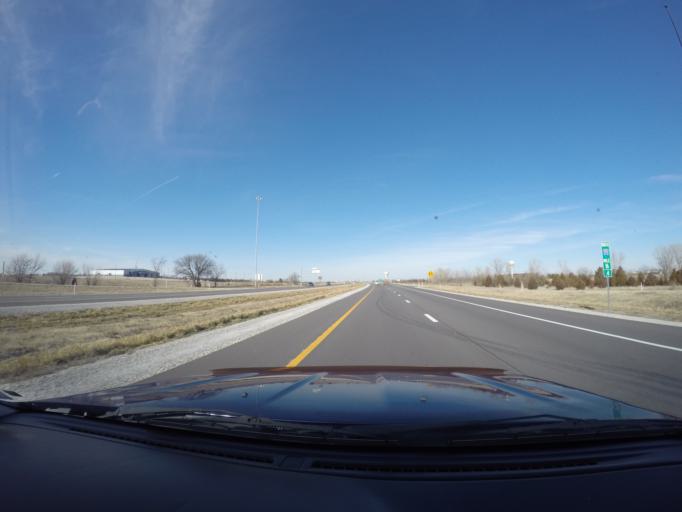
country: US
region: Kansas
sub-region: Sedgwick County
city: Park City
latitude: 37.8278
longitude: -97.3265
